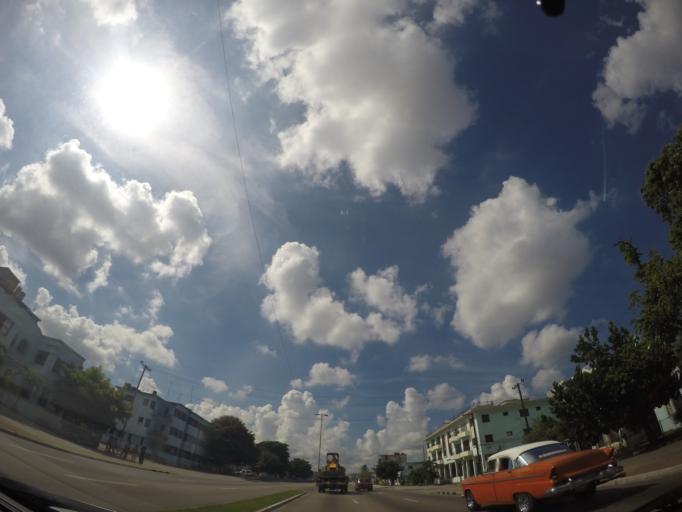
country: CU
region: La Habana
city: Cerro
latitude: 23.1098
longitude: -82.4184
